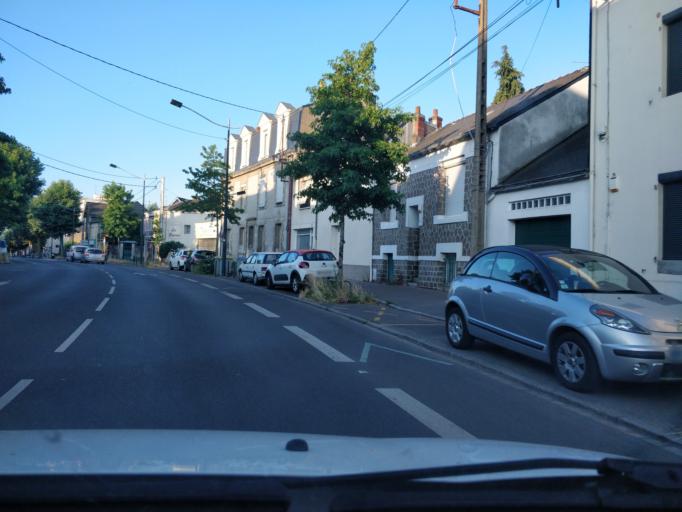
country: FR
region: Pays de la Loire
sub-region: Departement de la Loire-Atlantique
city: Nantes
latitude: 47.2371
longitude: -1.5633
